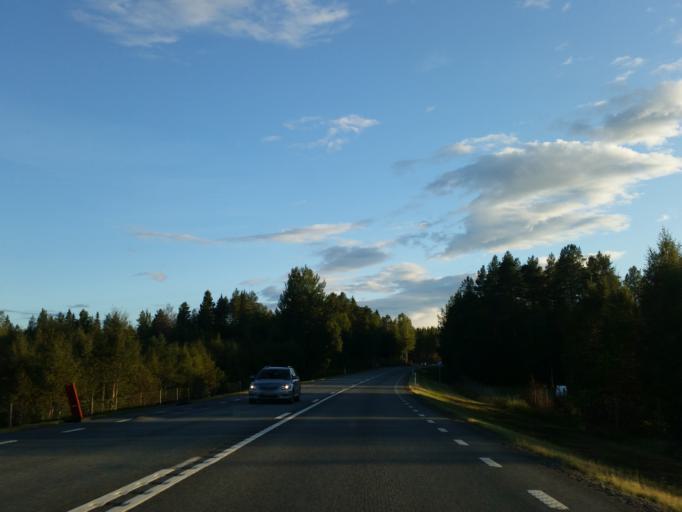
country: SE
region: Vaesterbotten
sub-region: Robertsfors Kommun
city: Robertsfors
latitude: 64.0218
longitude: 20.8390
